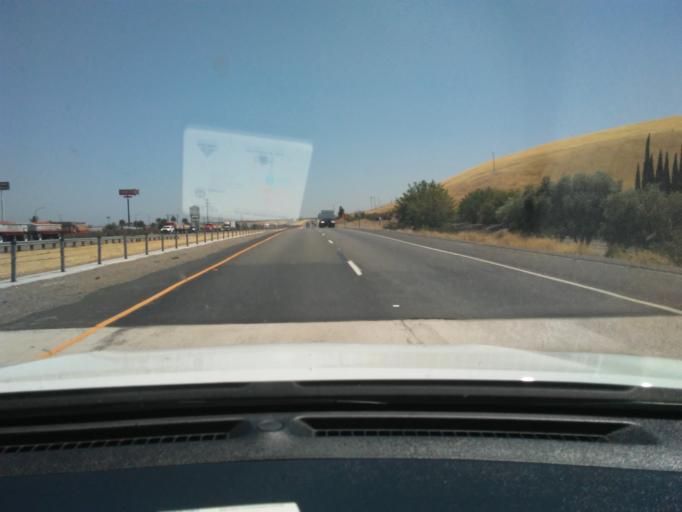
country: US
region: California
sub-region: Stanislaus County
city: Patterson
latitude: 37.5399
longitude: -121.2676
